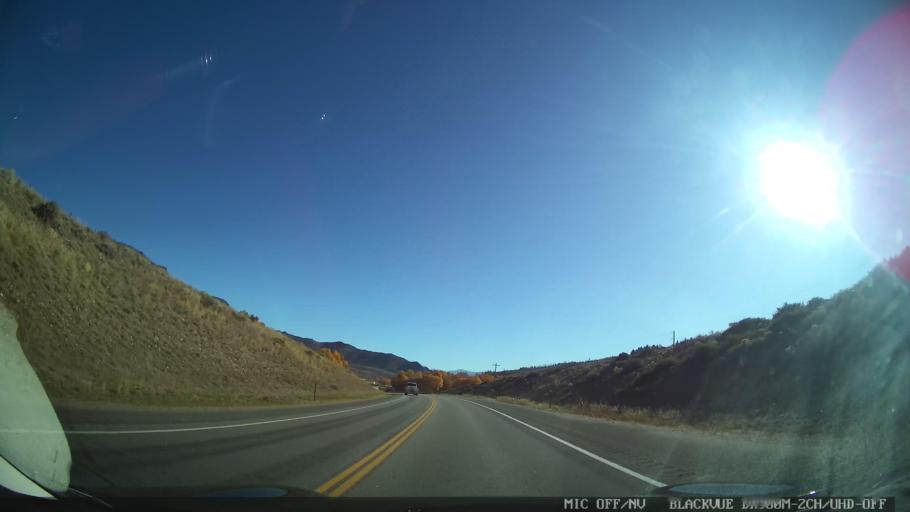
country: US
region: Colorado
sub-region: Grand County
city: Hot Sulphur Springs
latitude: 40.0995
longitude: -106.0334
